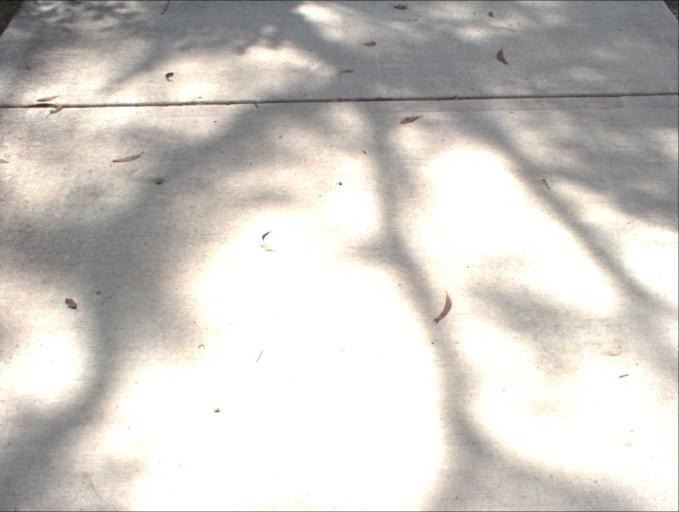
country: AU
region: Queensland
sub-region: Logan
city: Woodridge
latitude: -27.6559
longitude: 153.0666
